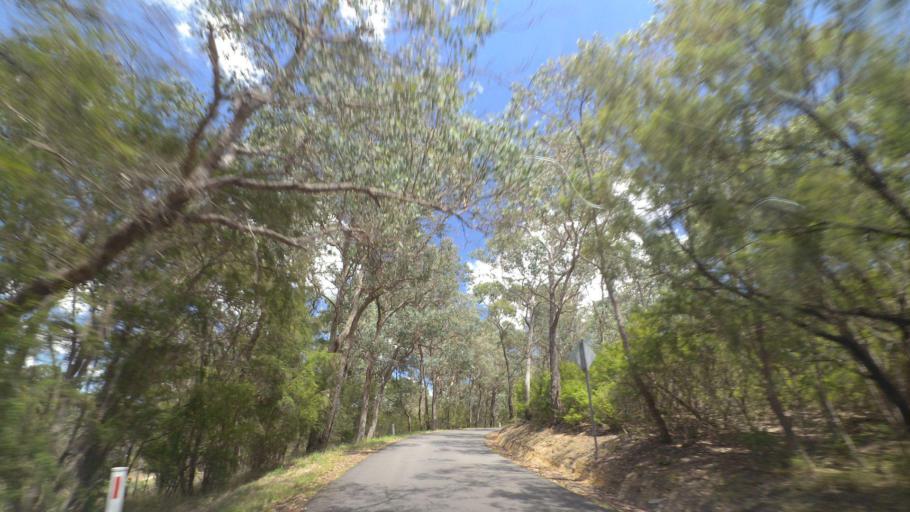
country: AU
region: Victoria
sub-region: Yarra Ranges
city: Chirnside Park
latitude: -37.7232
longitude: 145.2797
